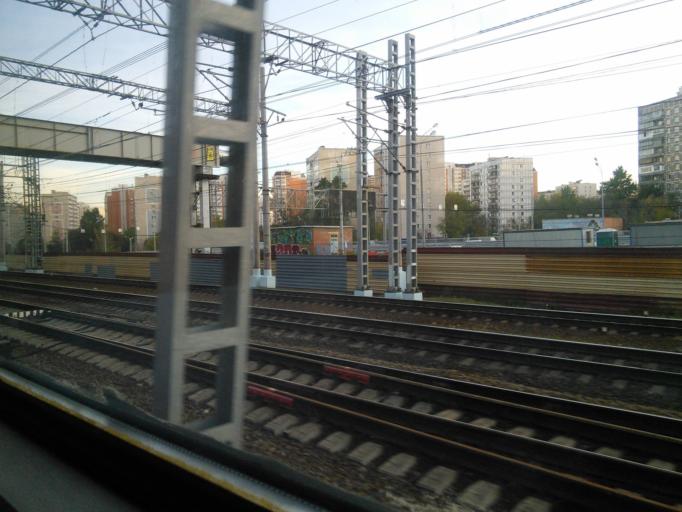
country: RU
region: Moscow
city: Businovo
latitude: 55.8766
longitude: 37.4934
